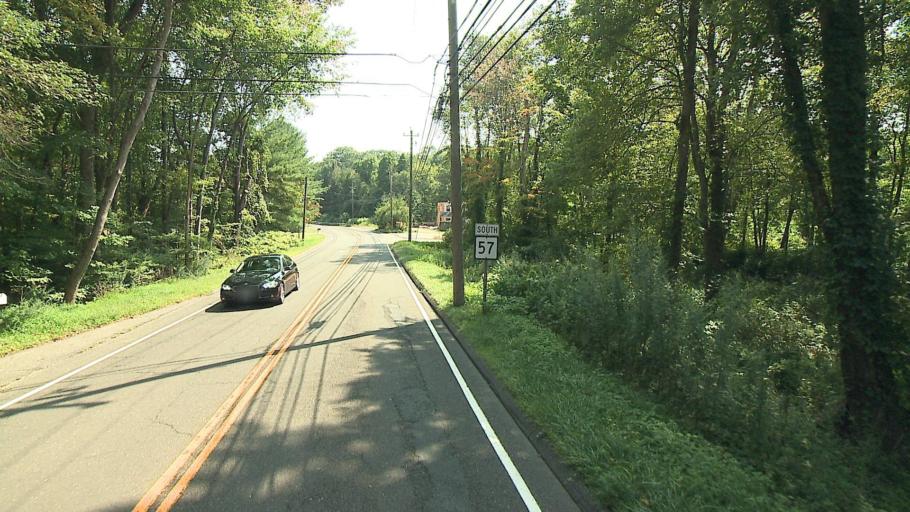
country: US
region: Connecticut
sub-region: Fairfield County
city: Georgetown
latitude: 41.2458
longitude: -73.4148
